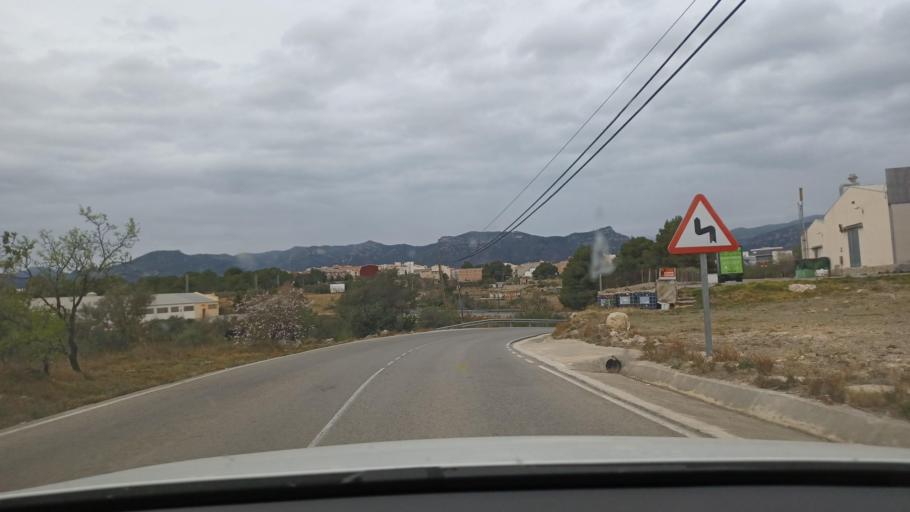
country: ES
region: Valencia
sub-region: Provincia de Castello
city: Rosell
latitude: 40.6293
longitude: 0.2920
